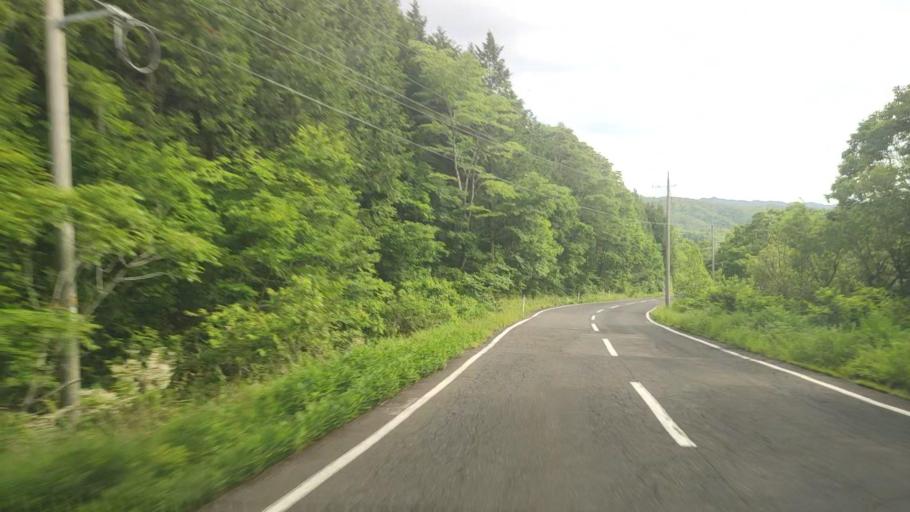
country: JP
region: Tottori
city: Kurayoshi
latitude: 35.3099
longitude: 134.0012
